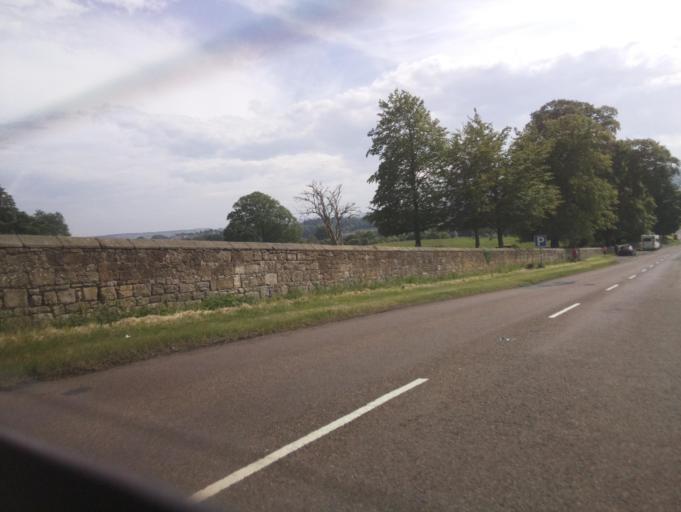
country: GB
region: England
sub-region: Northumberland
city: Alnwick
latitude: 55.4262
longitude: -1.7012
